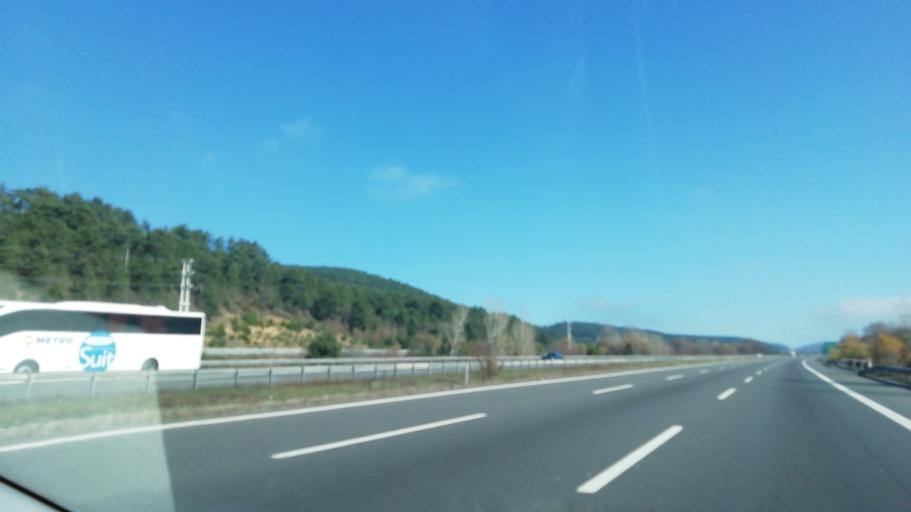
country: TR
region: Bolu
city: Gokcesu
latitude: 40.7415
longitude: 31.8459
